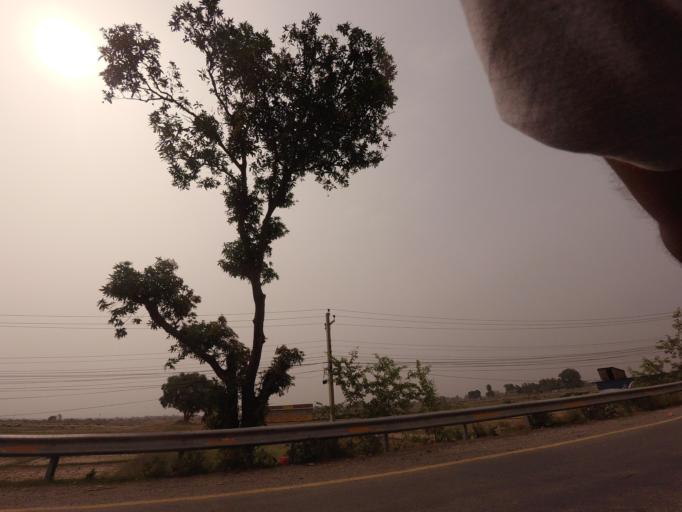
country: NP
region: Western Region
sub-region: Lumbini Zone
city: Bhairahawa
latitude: 27.5096
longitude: 83.3886
